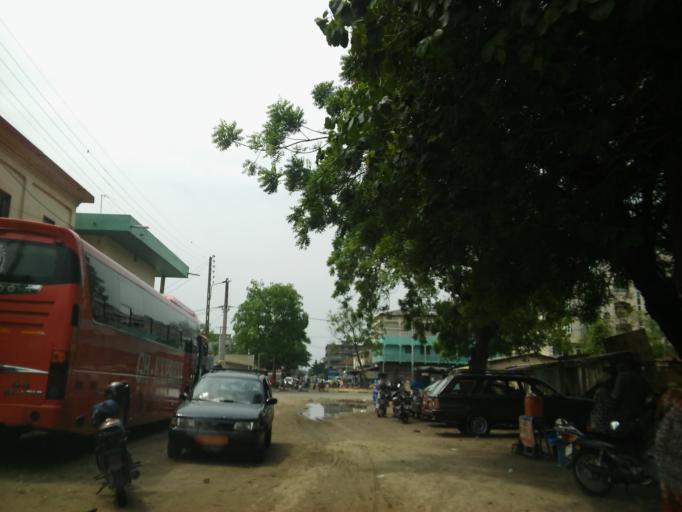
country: BJ
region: Littoral
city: Cotonou
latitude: 6.3612
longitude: 2.4330
